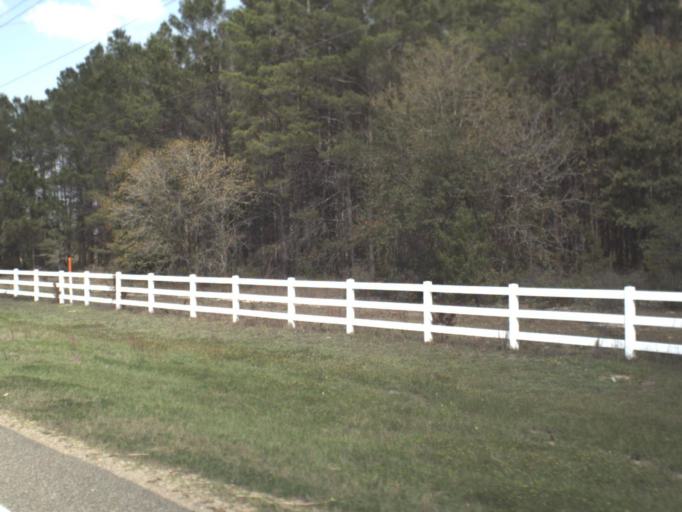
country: US
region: Florida
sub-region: Liberty County
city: Bristol
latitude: 30.4222
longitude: -84.9091
